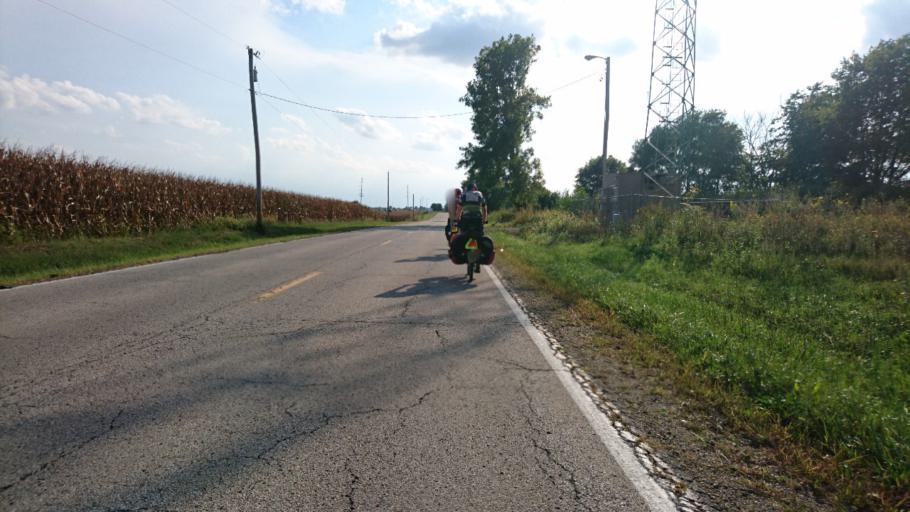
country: US
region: Illinois
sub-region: Logan County
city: Atlanta
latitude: 40.3062
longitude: -89.1792
